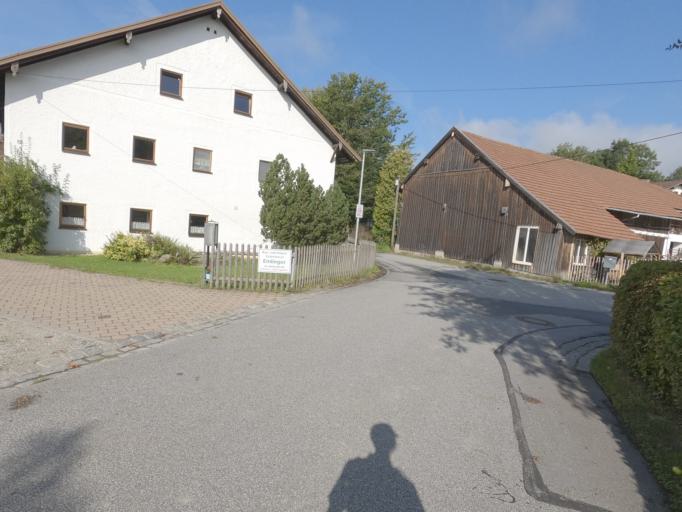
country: DE
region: Bavaria
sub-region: Lower Bavaria
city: Niederalteich
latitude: 48.8157
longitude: 13.0230
